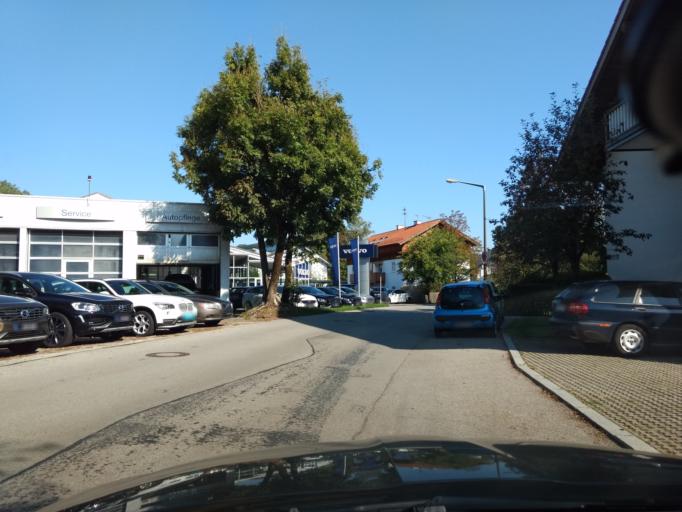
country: DE
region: Bavaria
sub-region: Upper Bavaria
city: Wolfratshausen
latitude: 47.9090
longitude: 11.4222
